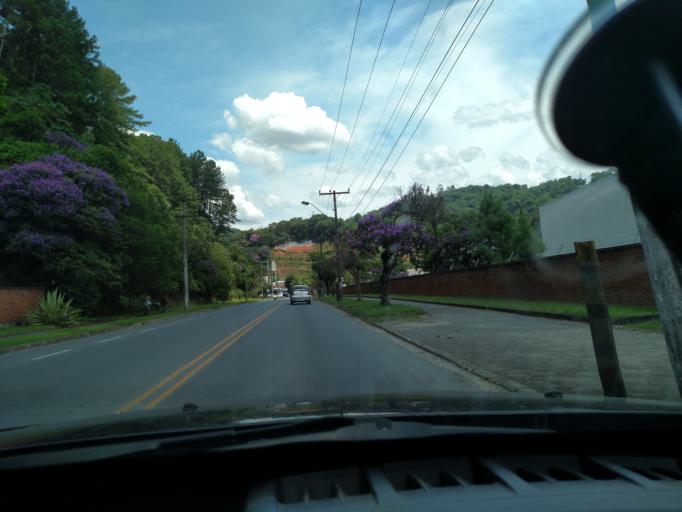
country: BR
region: Santa Catarina
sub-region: Blumenau
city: Blumenau
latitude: -26.9593
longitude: -49.0655
